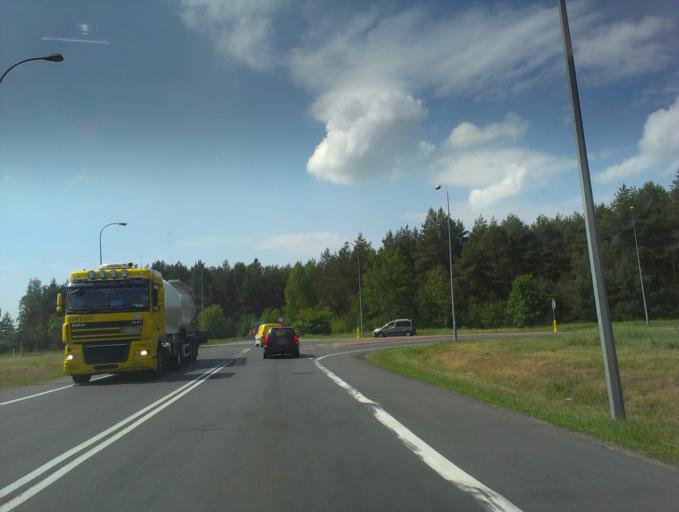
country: PL
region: Greater Poland Voivodeship
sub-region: Powiat pilski
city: Pila
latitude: 53.1237
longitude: 16.7735
